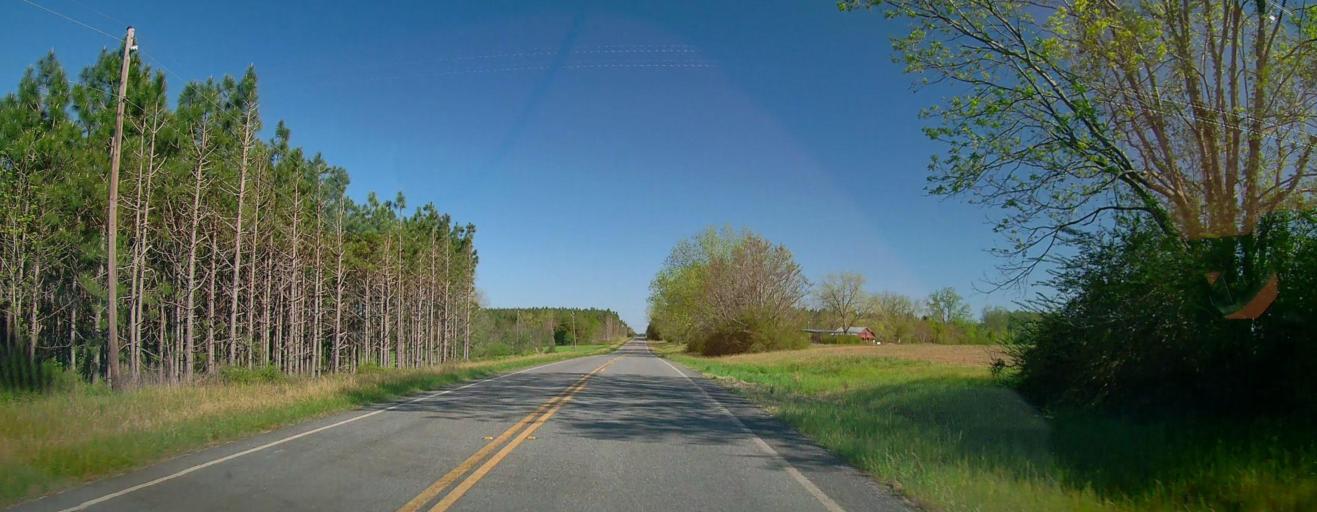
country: US
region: Georgia
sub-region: Wilcox County
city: Rochelle
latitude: 31.9998
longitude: -83.4787
